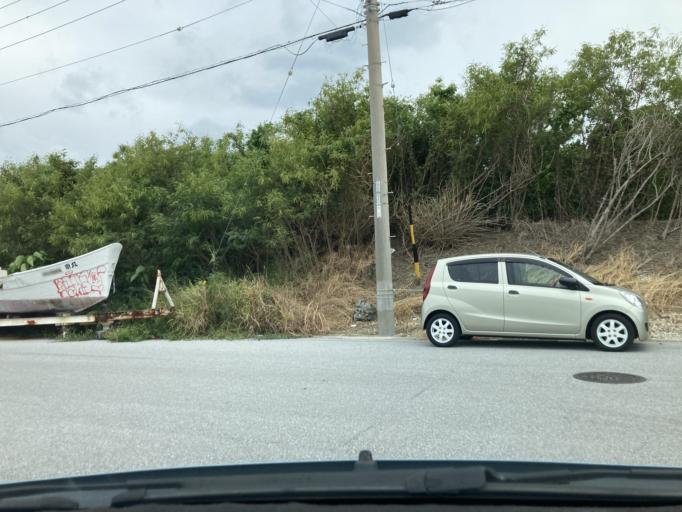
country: JP
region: Okinawa
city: Itoman
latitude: 26.1277
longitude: 127.6540
